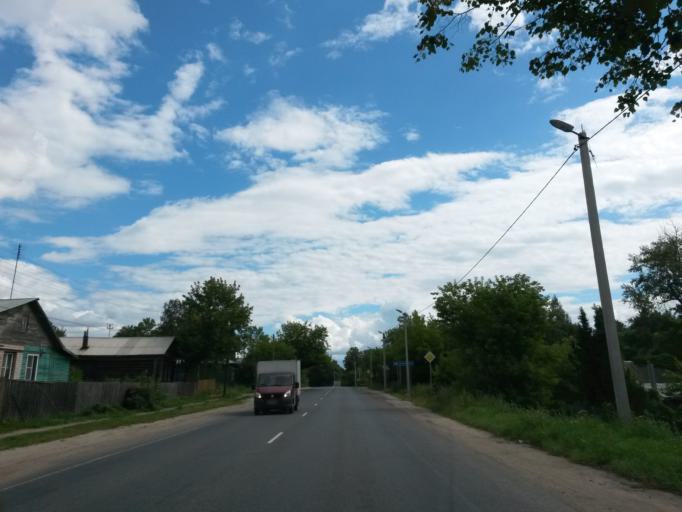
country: RU
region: Ivanovo
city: Novo-Talitsy
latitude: 57.0655
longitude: 40.7045
